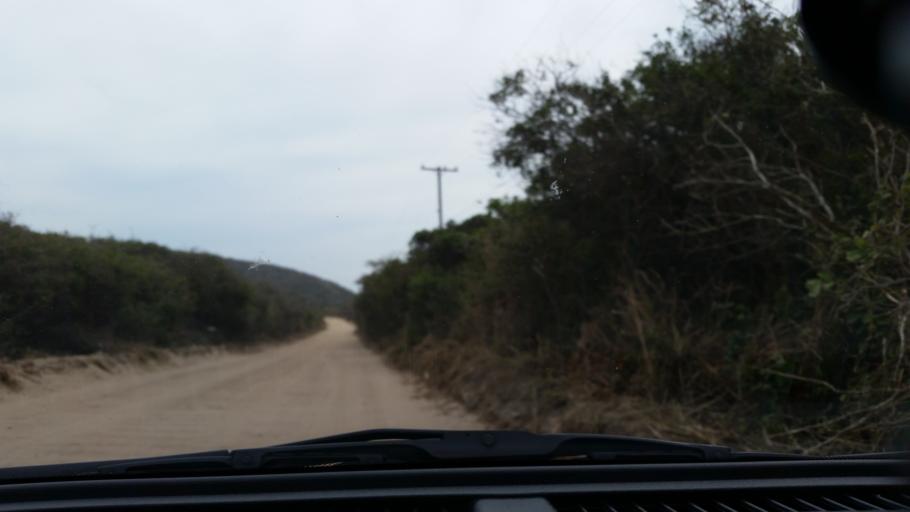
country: BR
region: Rio de Janeiro
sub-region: Cabo Frio
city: Cabo Frio
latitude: -22.8715
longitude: -41.9842
